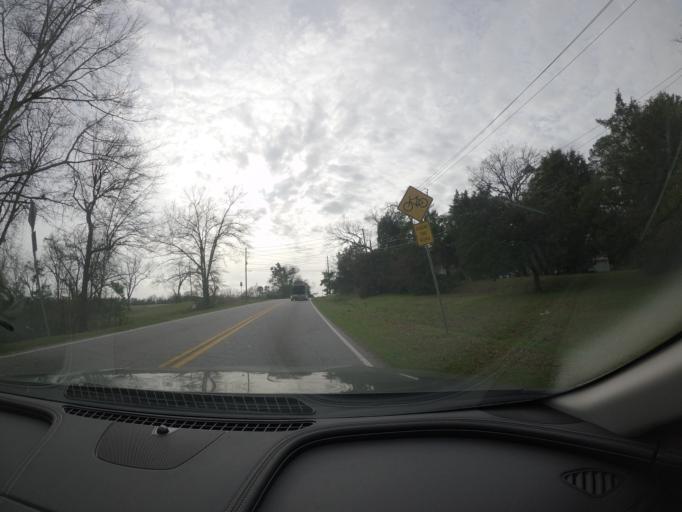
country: US
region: Georgia
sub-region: Columbia County
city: Grovetown
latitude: 33.4705
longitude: -82.1542
